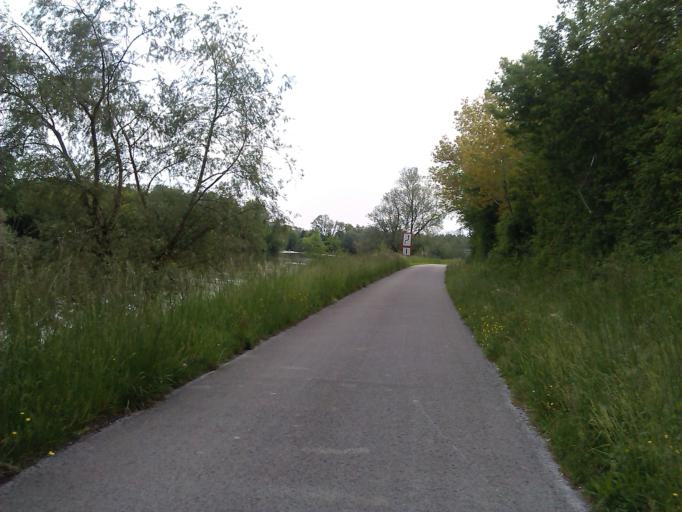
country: FR
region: Franche-Comte
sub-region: Departement du Jura
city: Dampierre
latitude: 47.1493
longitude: 5.7307
